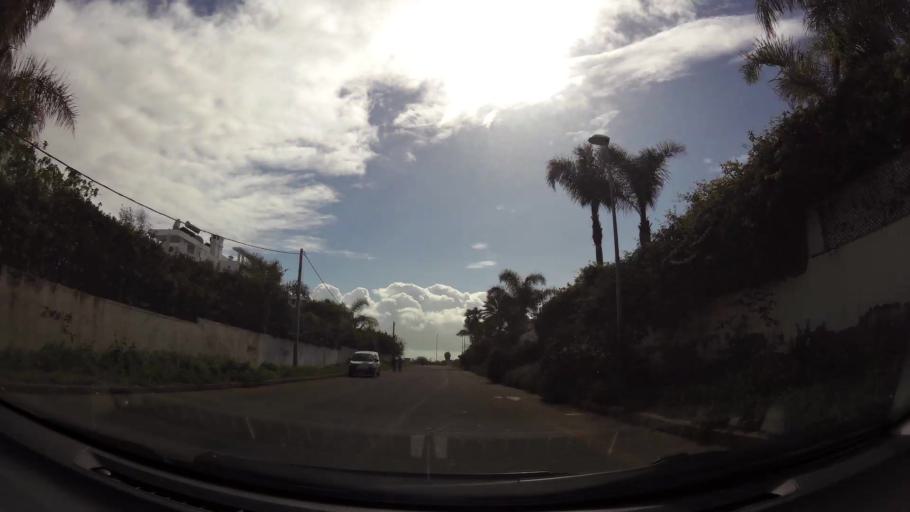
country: MA
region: Grand Casablanca
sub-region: Casablanca
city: Casablanca
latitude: 33.5707
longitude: -7.7070
